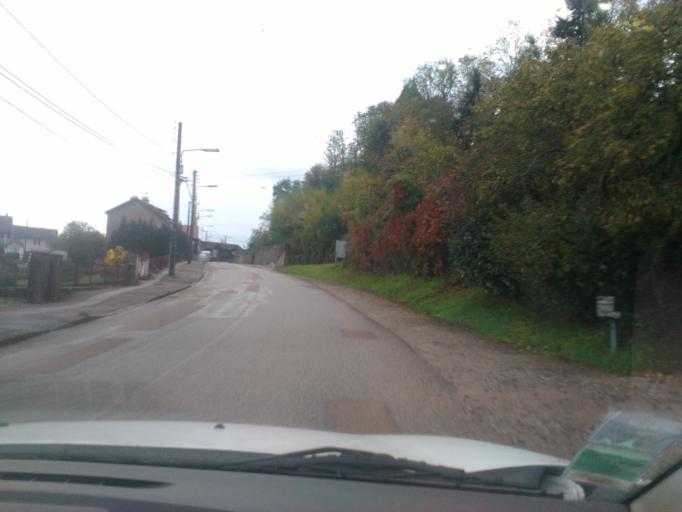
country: FR
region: Lorraine
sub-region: Departement des Vosges
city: Bruyeres
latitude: 48.2140
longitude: 6.7208
